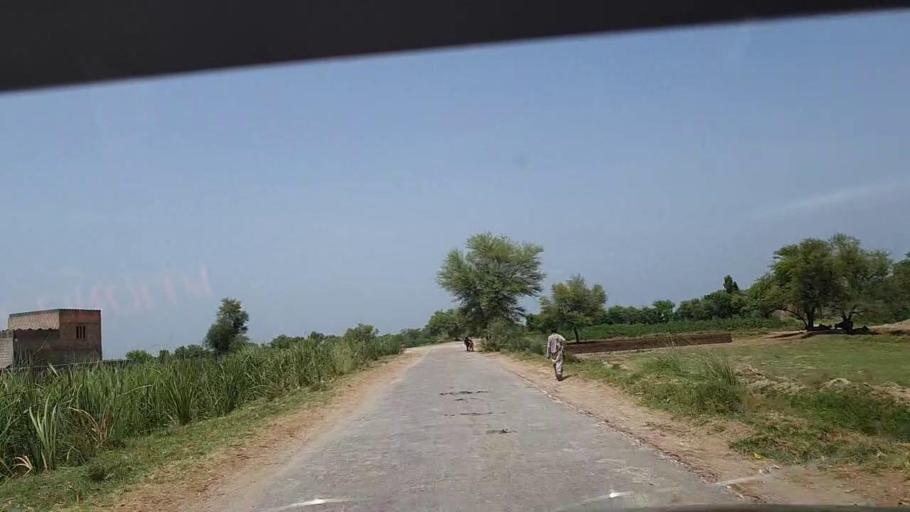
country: PK
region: Sindh
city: Khanpur
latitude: 27.8023
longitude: 69.4507
